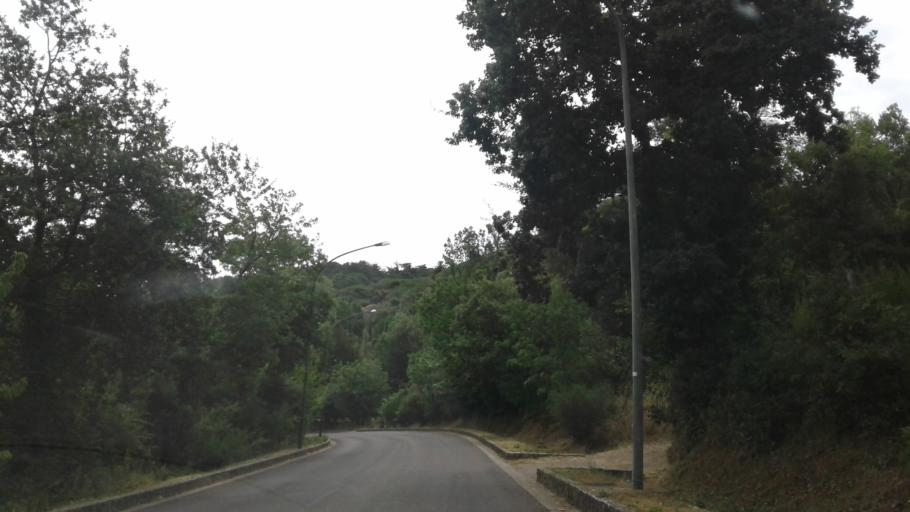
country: IT
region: Sardinia
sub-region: Provincia di Olbia-Tempio
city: Tempio Pausania
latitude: 40.9004
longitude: 9.0946
